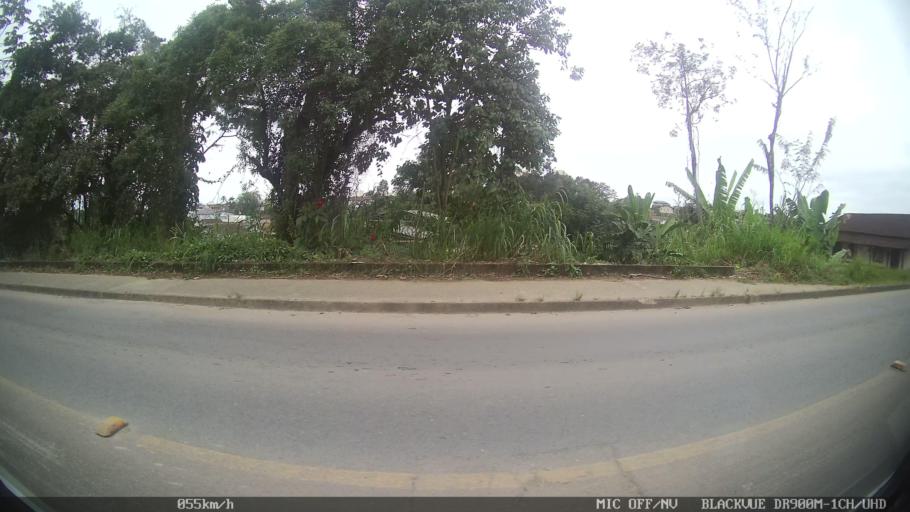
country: BR
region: Santa Catarina
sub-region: Joinville
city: Joinville
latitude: -26.3340
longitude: -48.8055
